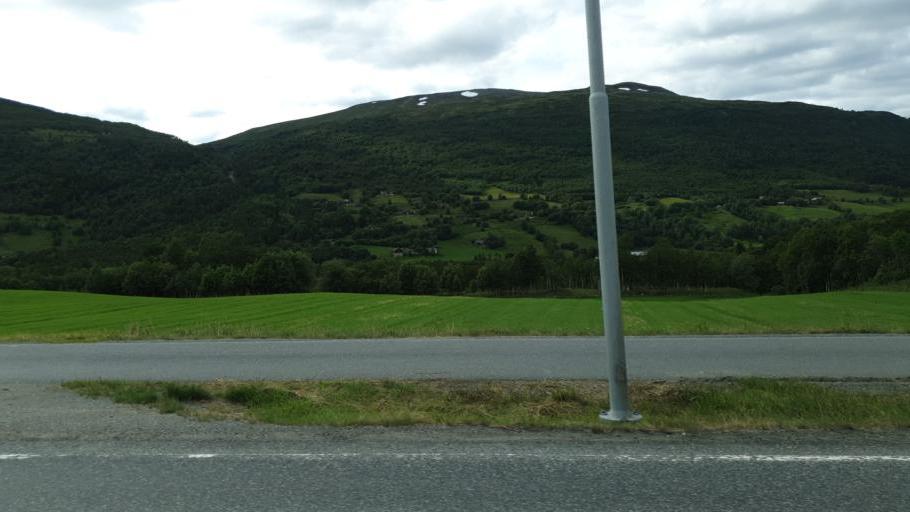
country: NO
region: Sor-Trondelag
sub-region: Oppdal
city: Oppdal
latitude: 62.5290
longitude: 9.6123
